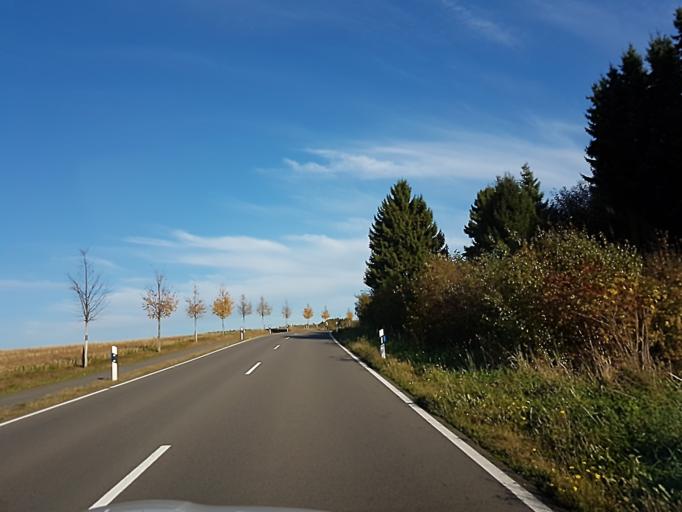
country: DE
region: North Rhine-Westphalia
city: Kierspe
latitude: 51.0961
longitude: 7.5780
